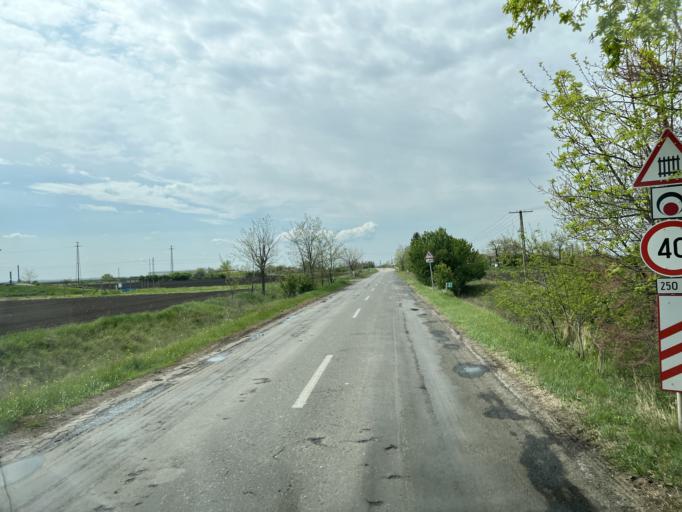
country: HU
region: Pest
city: Abony
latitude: 47.1763
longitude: 19.9901
